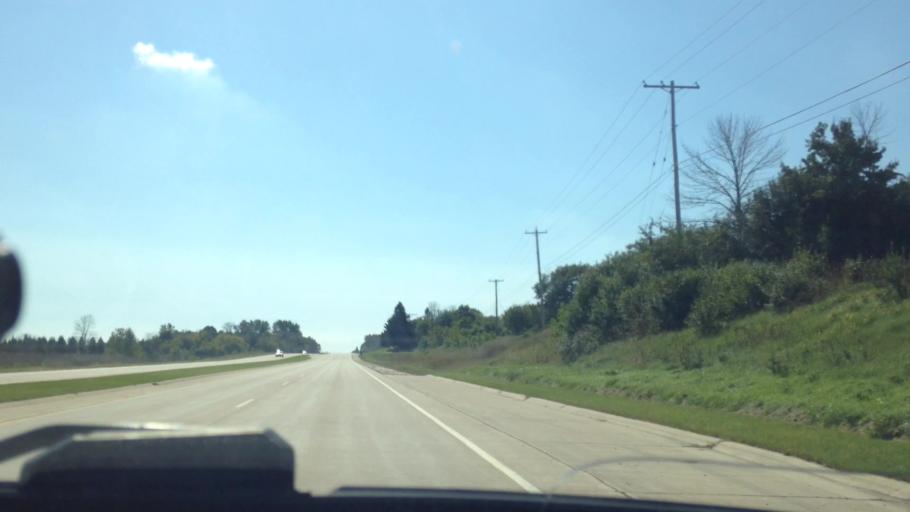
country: US
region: Wisconsin
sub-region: Ozaukee County
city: Saukville
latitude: 43.3616
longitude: -87.9072
